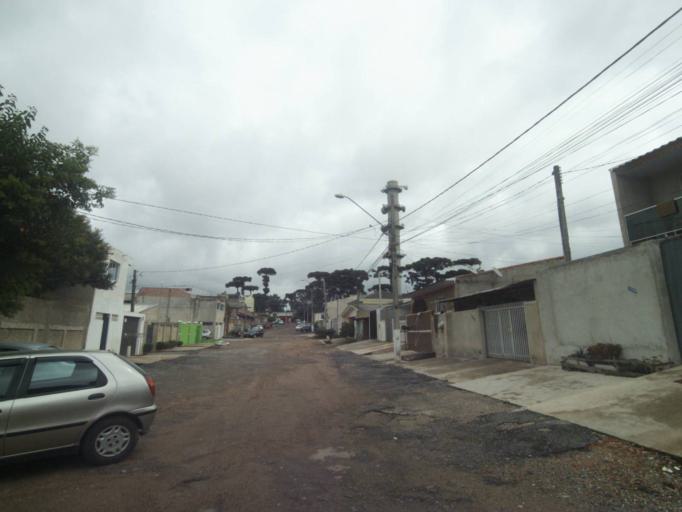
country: BR
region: Parana
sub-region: Curitiba
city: Curitiba
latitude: -25.4964
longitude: -49.3009
